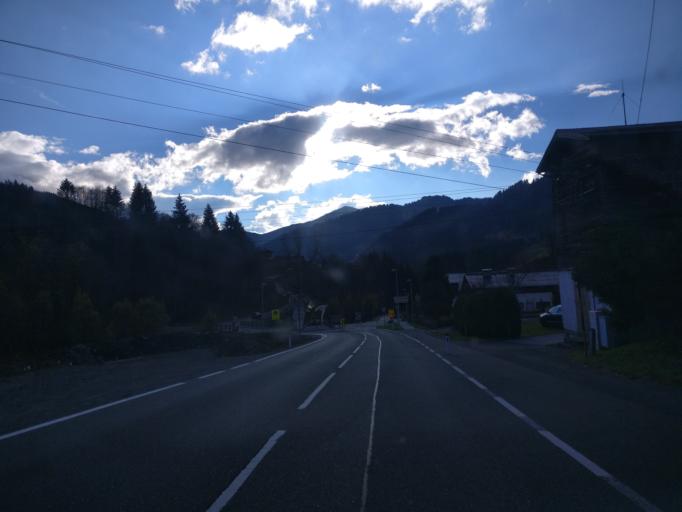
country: AT
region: Salzburg
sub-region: Politischer Bezirk Zell am See
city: Dienten am Hochkonig
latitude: 47.3886
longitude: 13.0145
